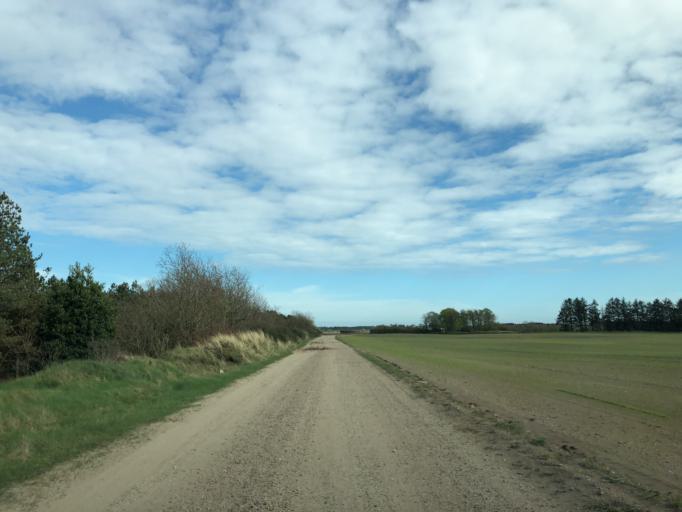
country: DK
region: Central Jutland
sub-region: Holstebro Kommune
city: Ulfborg
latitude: 56.2448
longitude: 8.3419
